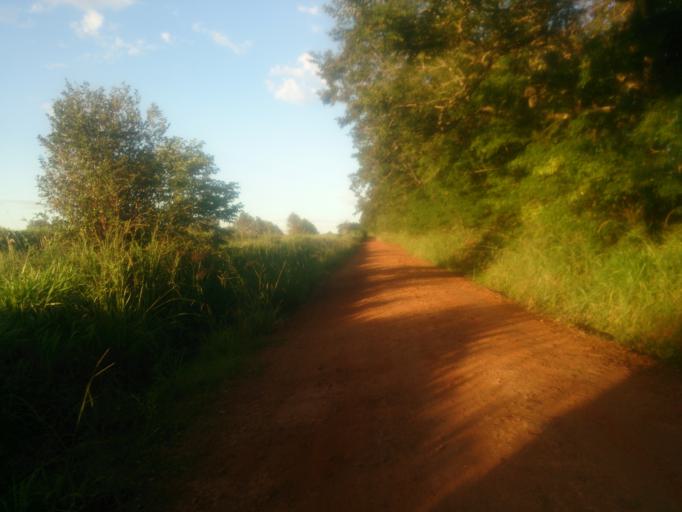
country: AR
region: Misiones
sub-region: Departamento de Obera
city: Obera
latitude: -27.4545
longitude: -55.1052
